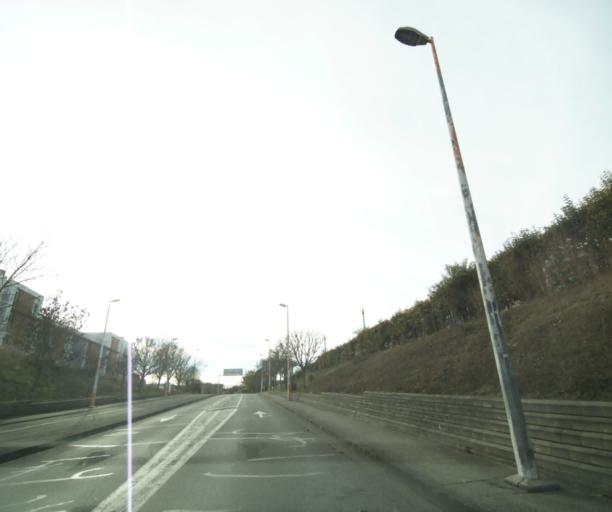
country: FR
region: Midi-Pyrenees
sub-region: Departement de la Haute-Garonne
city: Ramonville-Saint-Agne
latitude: 43.5786
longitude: 1.4721
